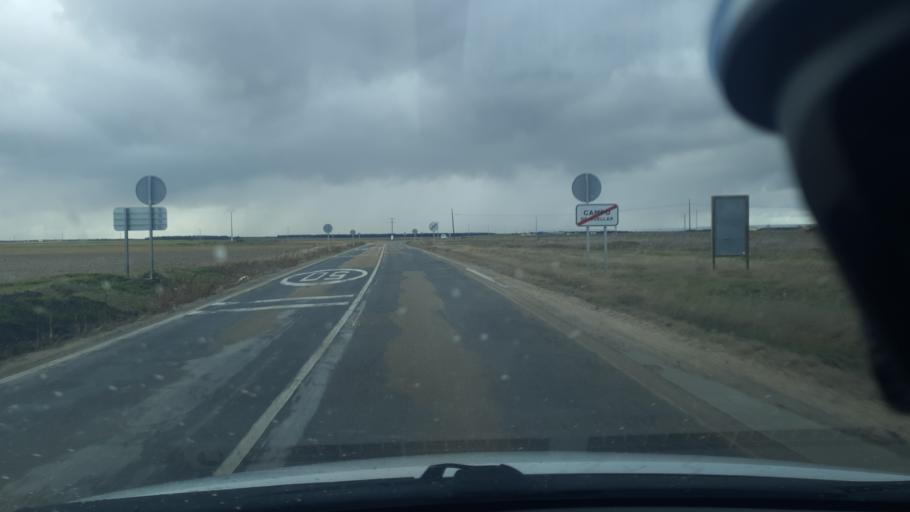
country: ES
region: Castille and Leon
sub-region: Provincia de Segovia
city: Sanchonuno
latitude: 41.3111
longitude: -4.3676
